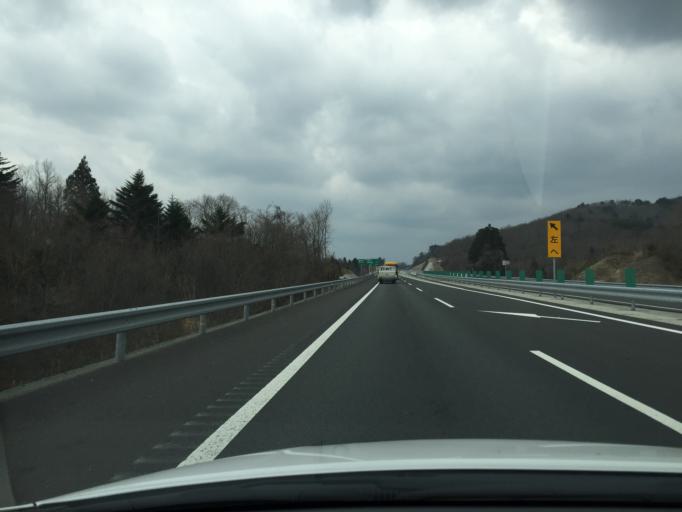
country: JP
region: Miyagi
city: Marumori
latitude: 37.8441
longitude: 140.8795
